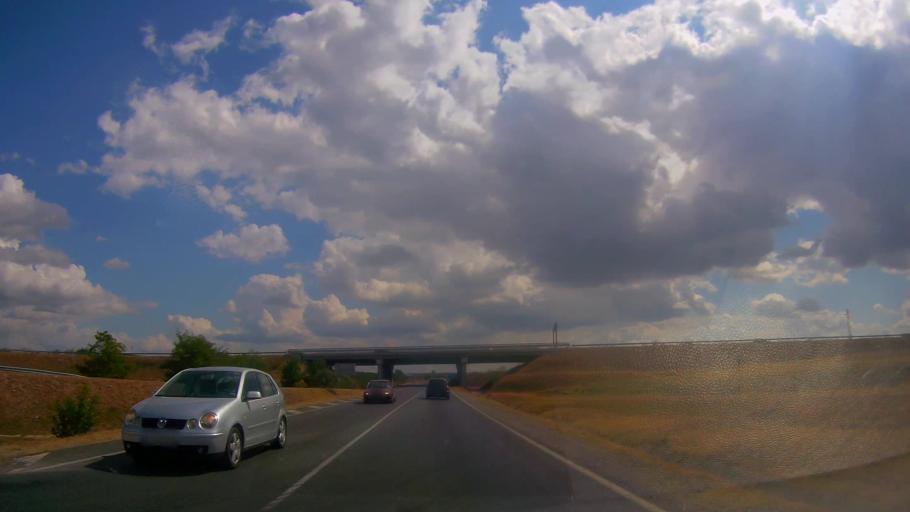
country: BG
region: Yambol
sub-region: Obshtina Yambol
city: Yambol
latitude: 42.5389
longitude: 26.4176
